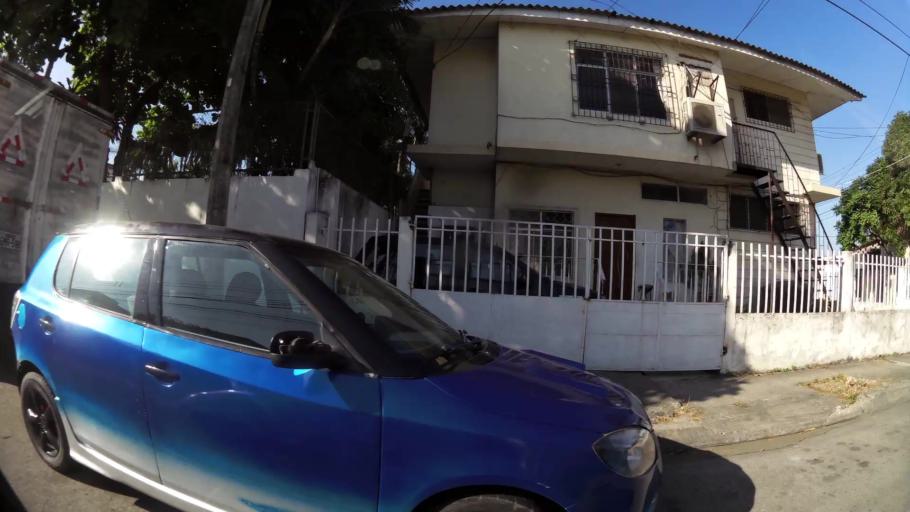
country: EC
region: Guayas
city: Eloy Alfaro
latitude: -2.1695
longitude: -79.8847
